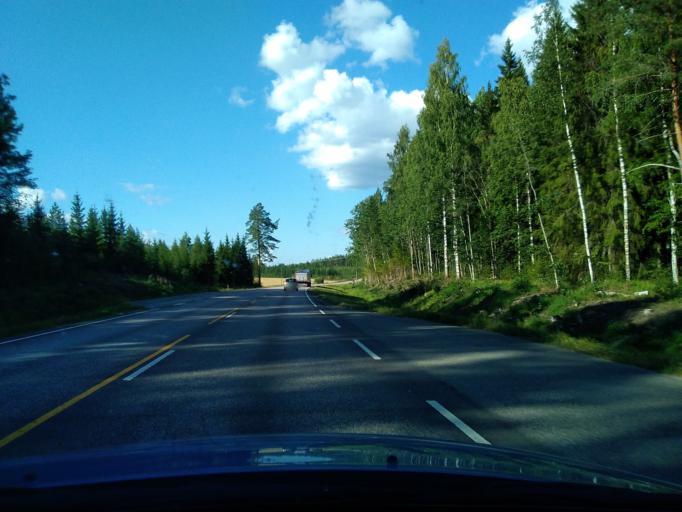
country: FI
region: Central Finland
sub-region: Keuruu
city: Keuruu
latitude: 62.1283
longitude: 24.7362
